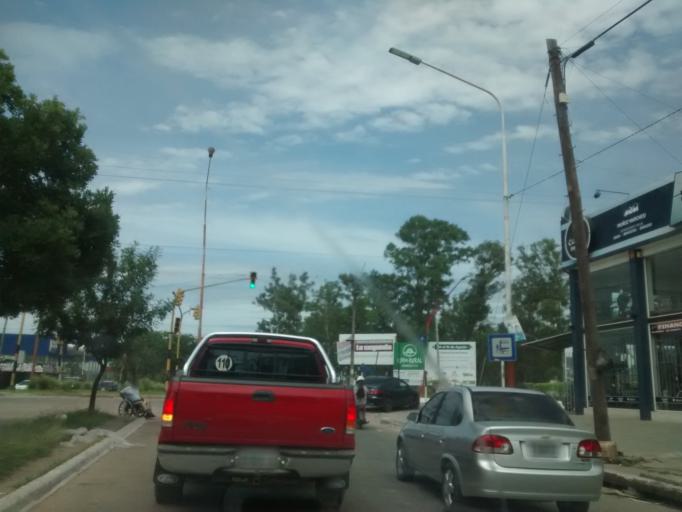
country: AR
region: Chaco
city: Resistencia
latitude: -27.4444
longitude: -59.0078
